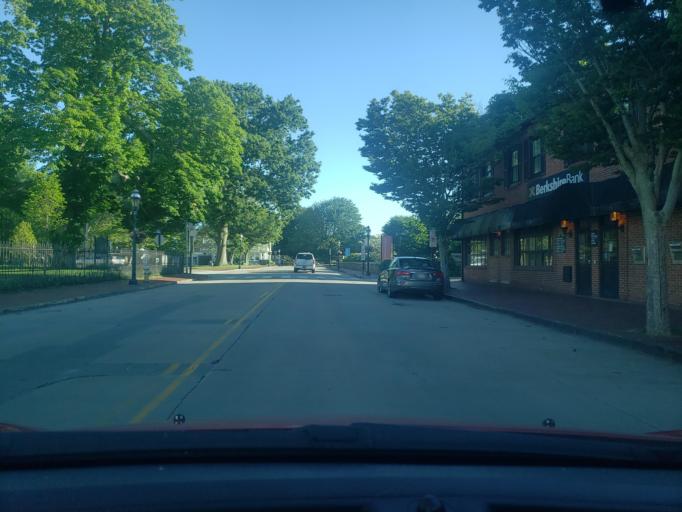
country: US
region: Rhode Island
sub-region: Newport County
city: Newport
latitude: 41.4848
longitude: -71.3087
